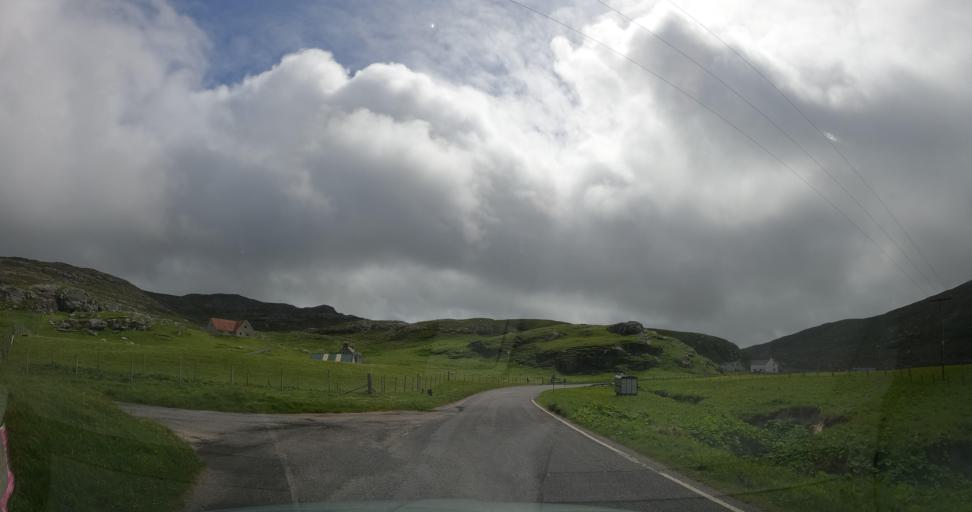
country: GB
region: Scotland
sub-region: Eilean Siar
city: Barra
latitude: 56.9727
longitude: -7.5155
